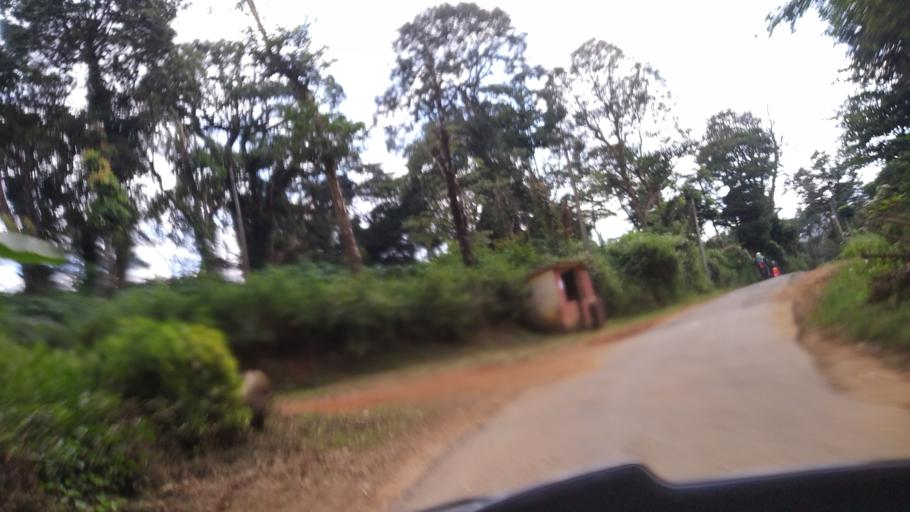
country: IN
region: Karnataka
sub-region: Kodagu
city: Ponnampet
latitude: 12.0366
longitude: 75.9105
